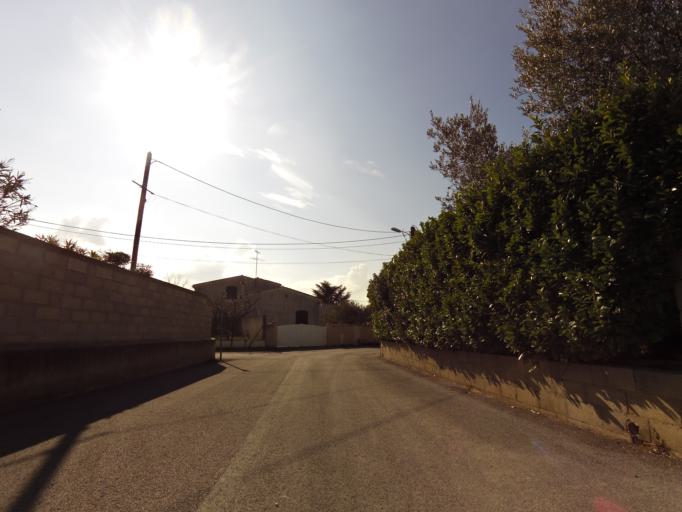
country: FR
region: Languedoc-Roussillon
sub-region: Departement du Gard
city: Codognan
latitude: 43.7259
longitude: 4.2240
